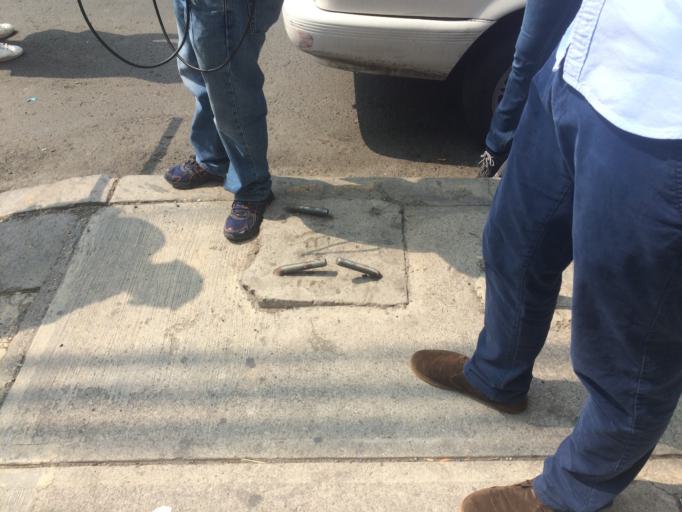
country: MX
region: Mexico City
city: Alvaro Obregon
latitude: 19.3833
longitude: -99.1972
